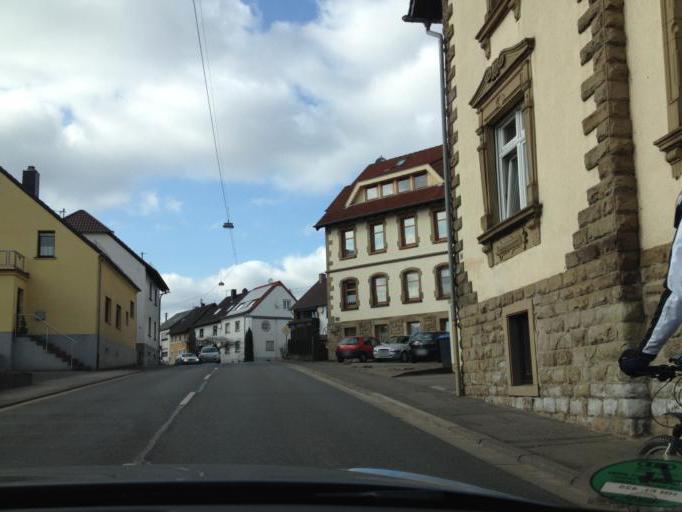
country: DE
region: Saarland
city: Oberthal
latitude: 49.4762
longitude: 7.1000
